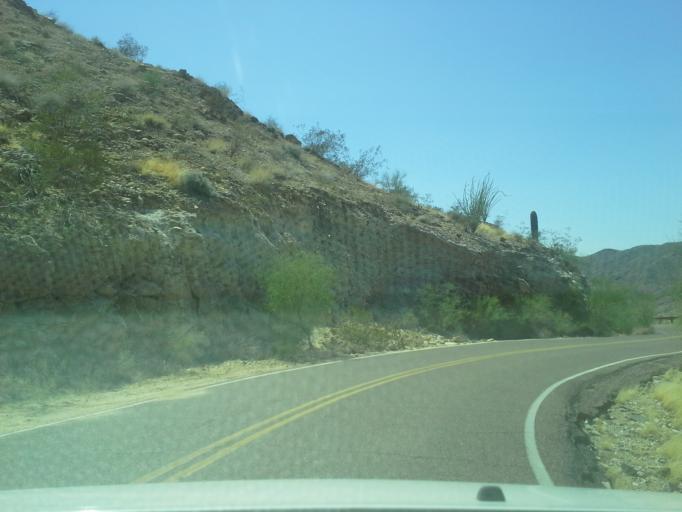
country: US
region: Arizona
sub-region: Maricopa County
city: Laveen
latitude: 33.3319
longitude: -112.0783
